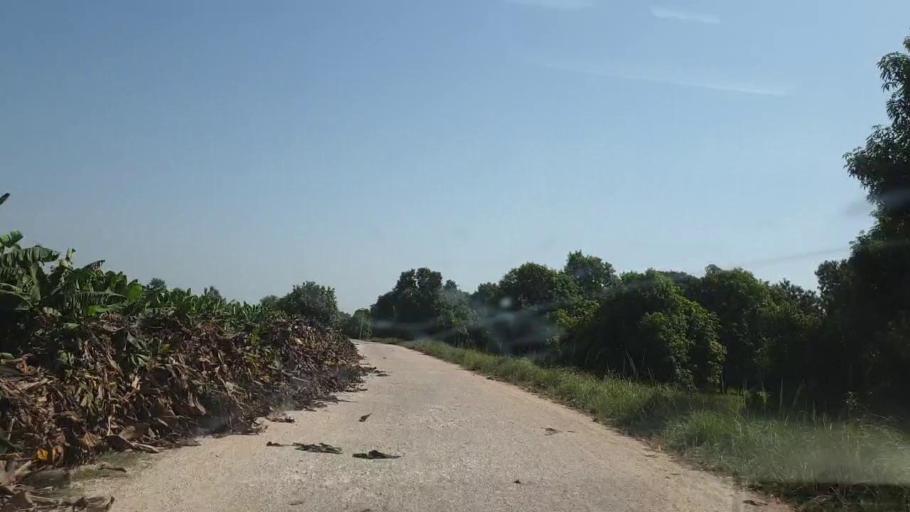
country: PK
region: Sindh
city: Tando Jam
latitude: 25.4059
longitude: 68.5823
